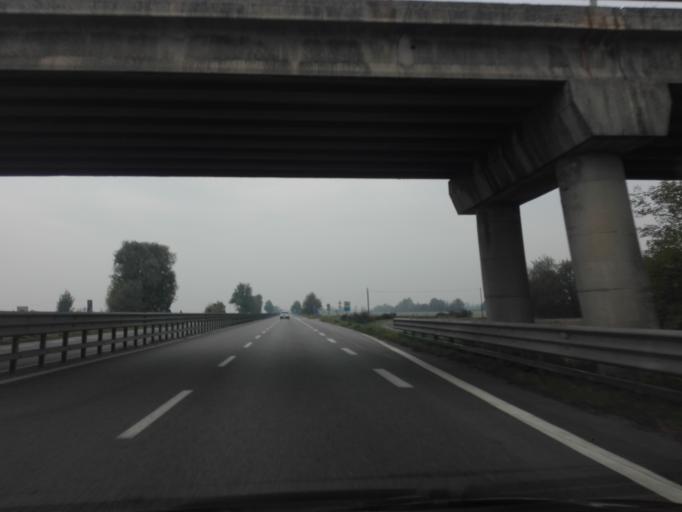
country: IT
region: Veneto
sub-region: Provincia di Rovigo
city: Fratta Polesine
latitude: 45.0234
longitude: 11.6235
